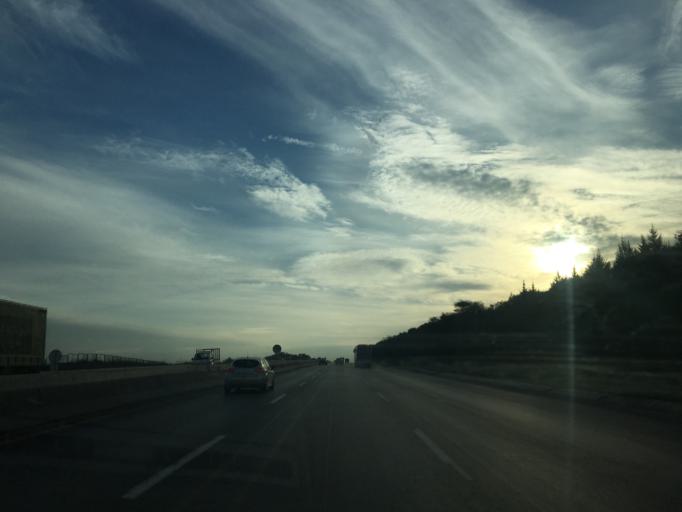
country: DZ
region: Bouira
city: Draa el Mizan
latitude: 36.4740
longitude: 3.7553
